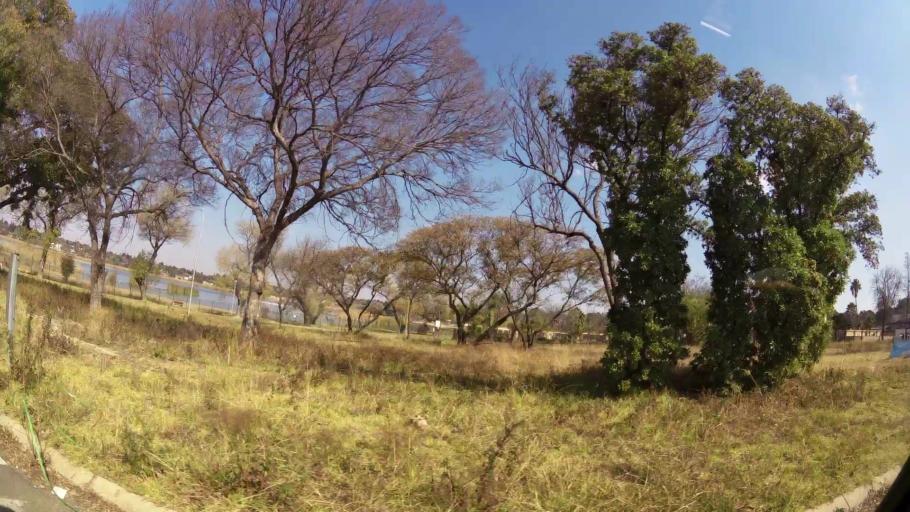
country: ZA
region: Gauteng
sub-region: Ekurhuleni Metropolitan Municipality
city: Benoni
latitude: -26.1887
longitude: 28.2932
